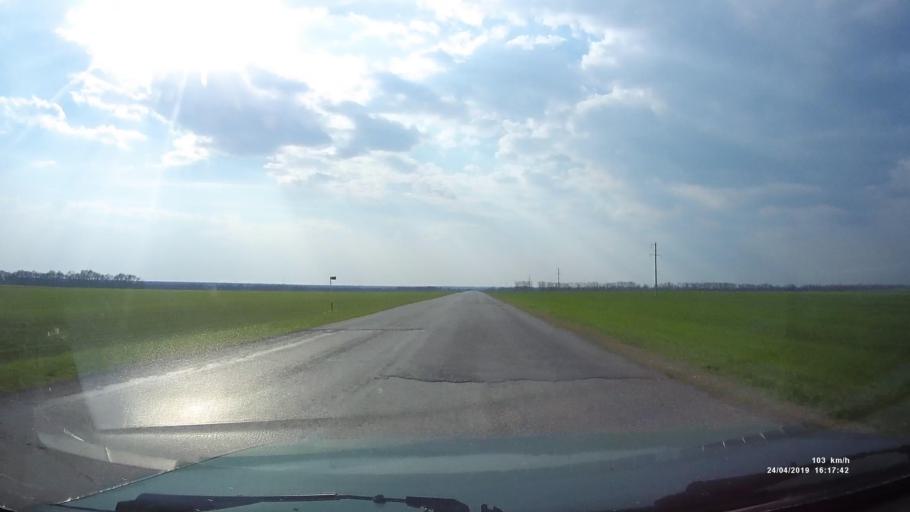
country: RU
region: Rostov
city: Sovetskoye
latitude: 46.7700
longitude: 42.1319
